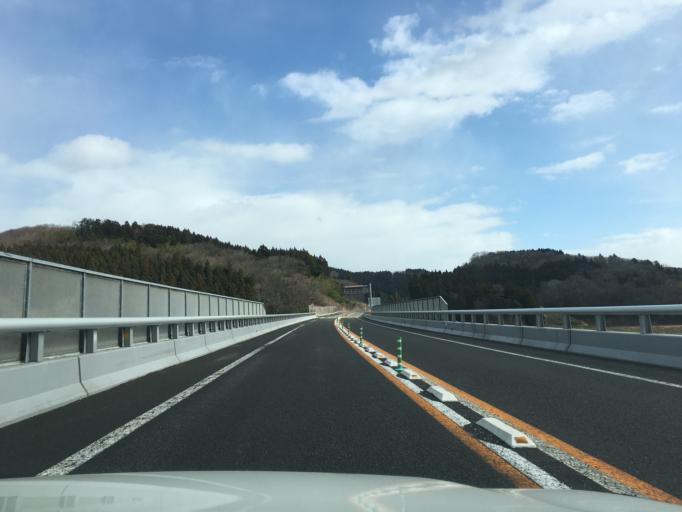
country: JP
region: Akita
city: Akita Shi
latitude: 39.5508
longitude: 140.0758
